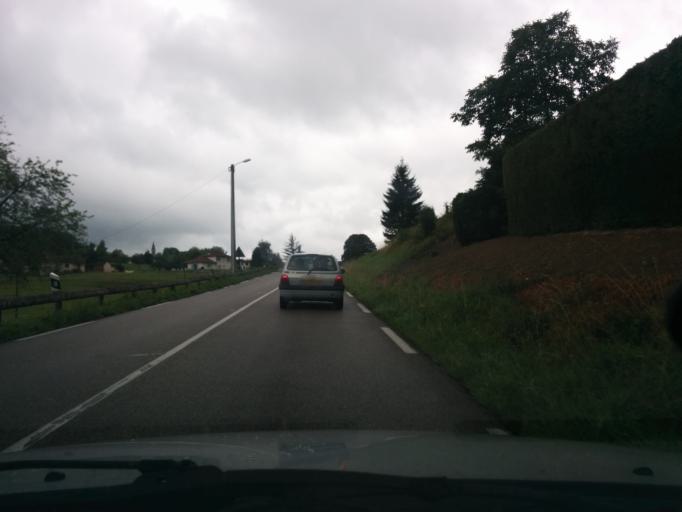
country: FR
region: Rhone-Alpes
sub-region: Departement de la Savoie
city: Saint-Beron
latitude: 45.4798
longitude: 5.6898
